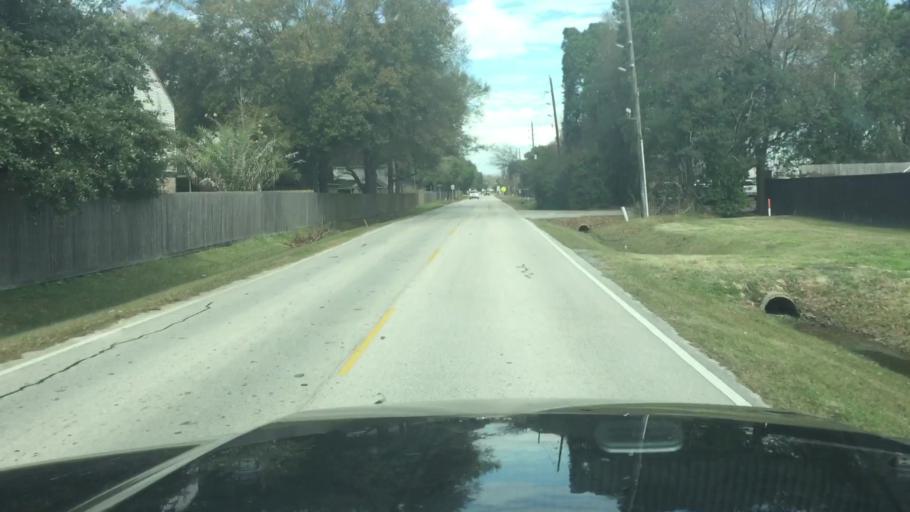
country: US
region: Texas
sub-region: Harris County
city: Oak Cliff Place
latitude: 29.8440
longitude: -95.6752
